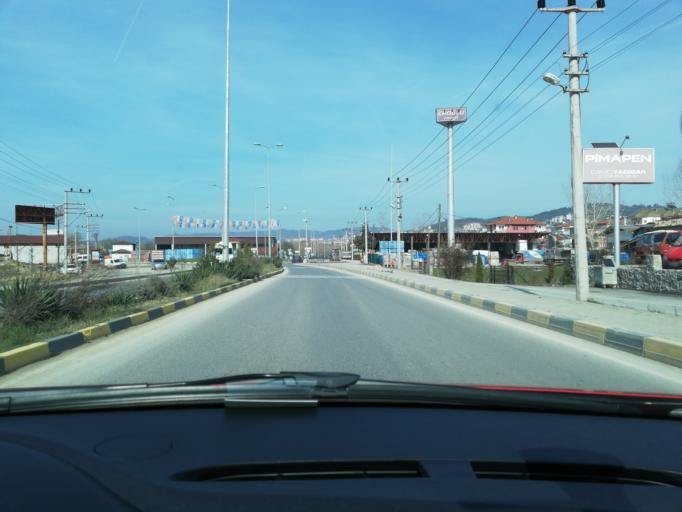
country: TR
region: Bartin
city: Bartin
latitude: 41.6302
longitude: 32.3511
